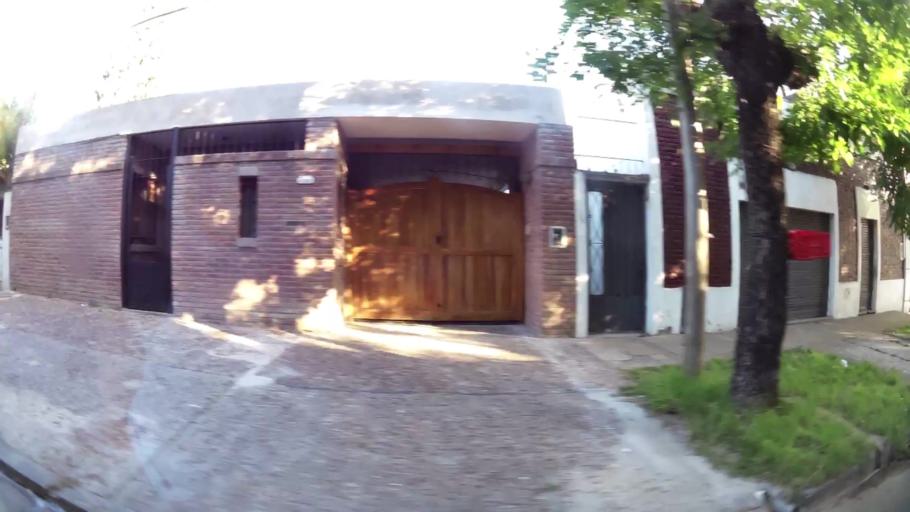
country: AR
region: Buenos Aires
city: Caseros
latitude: -34.5507
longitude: -58.5786
